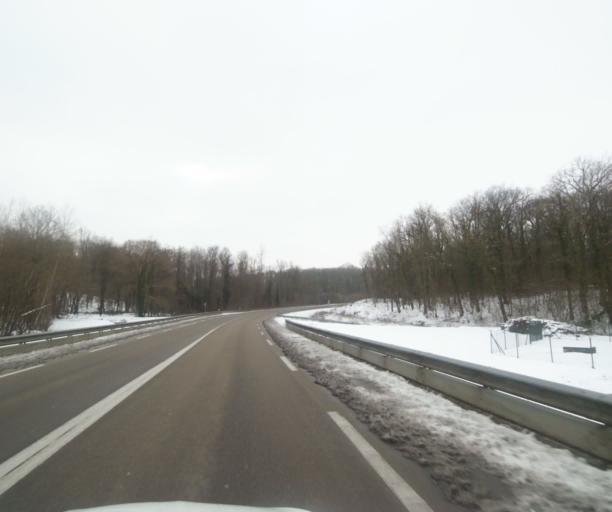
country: FR
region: Champagne-Ardenne
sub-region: Departement de la Haute-Marne
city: Saint-Dizier
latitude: 48.6153
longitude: 4.9177
